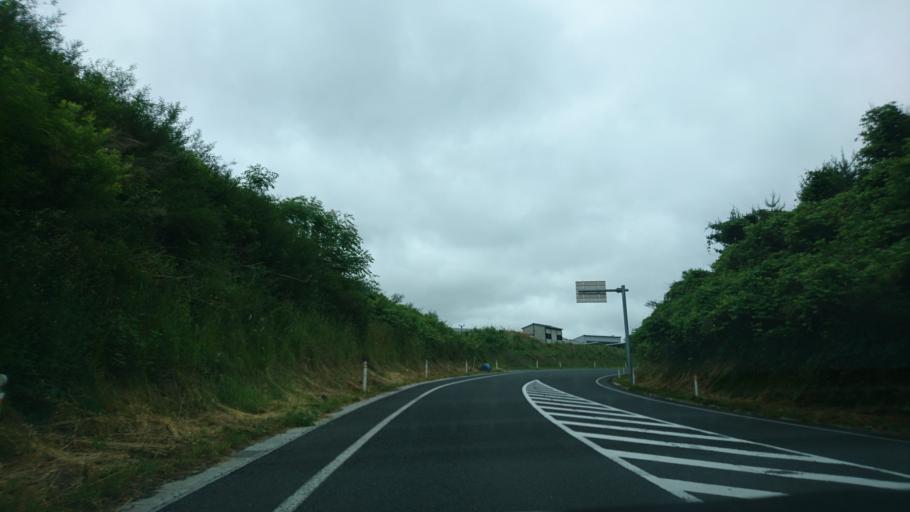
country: JP
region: Iwate
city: Ichinoseki
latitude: 38.9044
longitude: 141.1577
